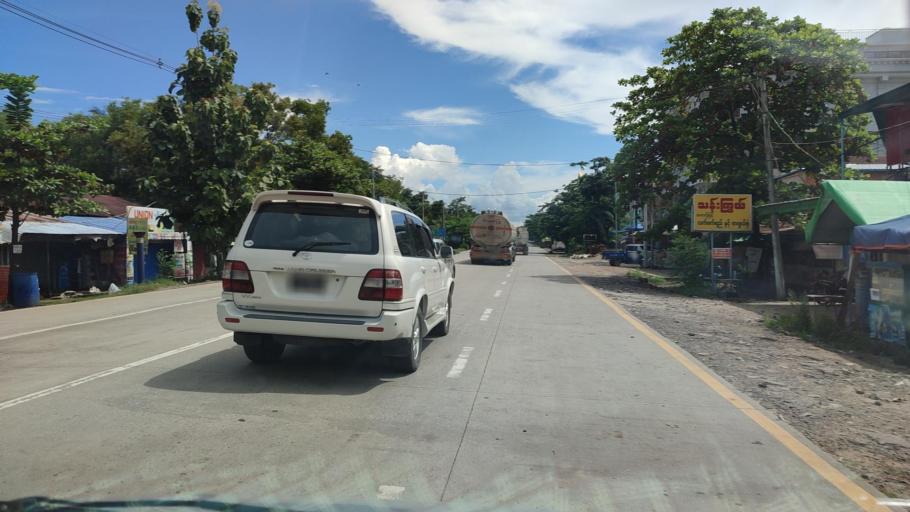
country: MM
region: Bago
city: Nyaunglebin
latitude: 17.9524
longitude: 96.7226
